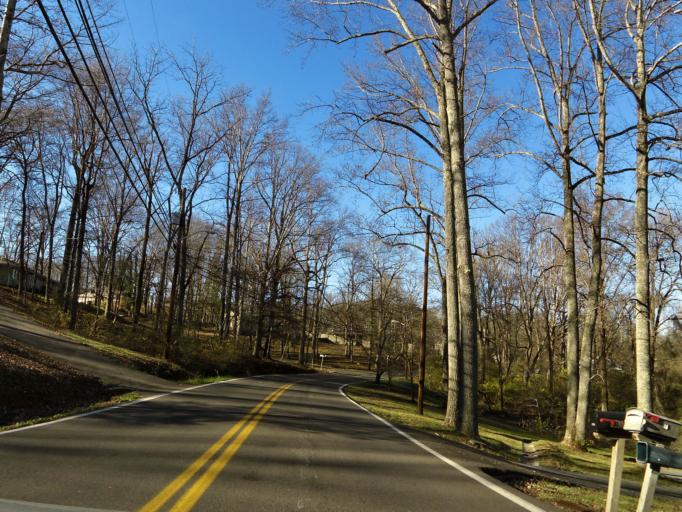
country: US
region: Tennessee
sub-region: Knox County
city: Knoxville
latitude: 36.0309
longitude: -83.9559
